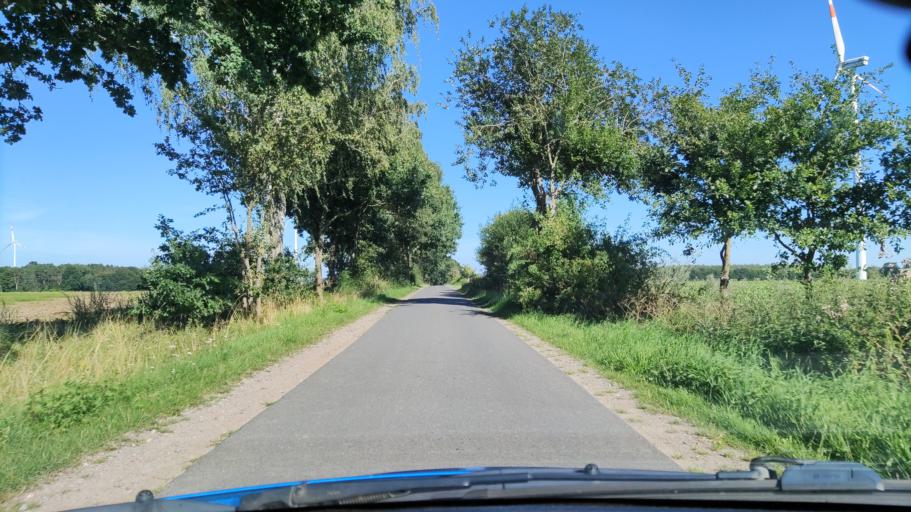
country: DE
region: Lower Saxony
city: Nahrendorf
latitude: 53.1797
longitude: 10.7891
